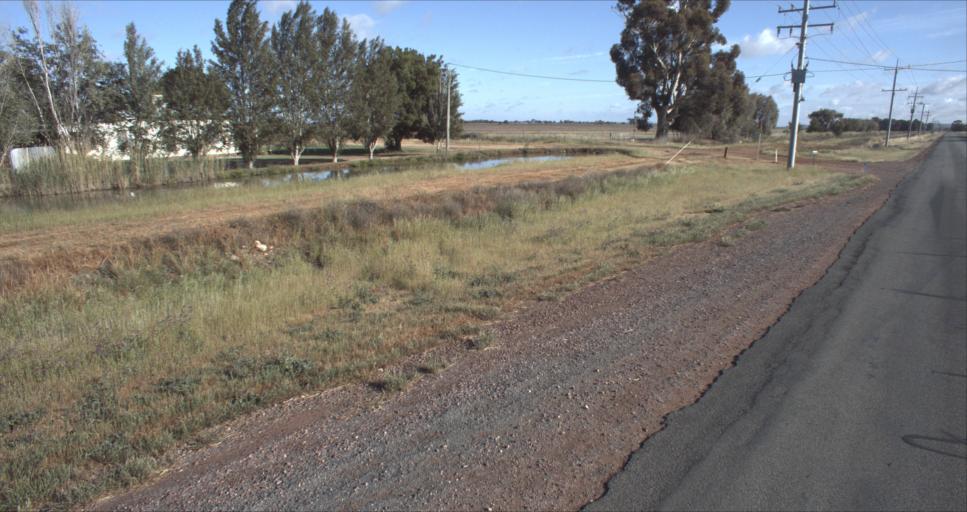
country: AU
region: New South Wales
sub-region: Leeton
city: Leeton
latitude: -34.5316
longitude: 146.3886
